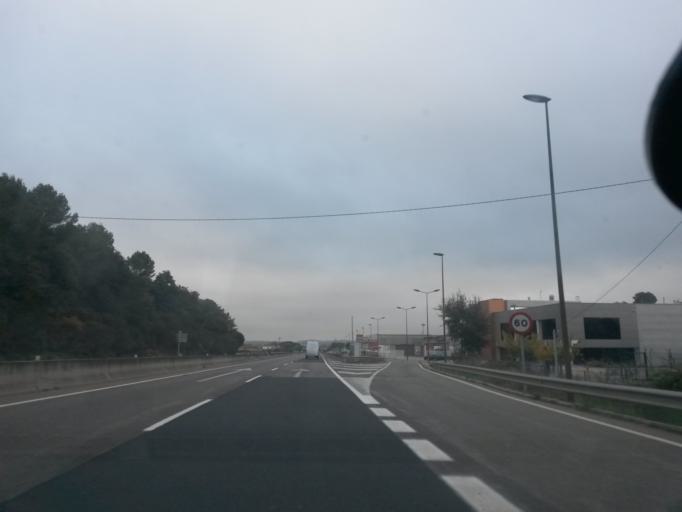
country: ES
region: Catalonia
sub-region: Provincia de Girona
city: Palol de Revardit
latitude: 42.0660
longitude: 2.8129
